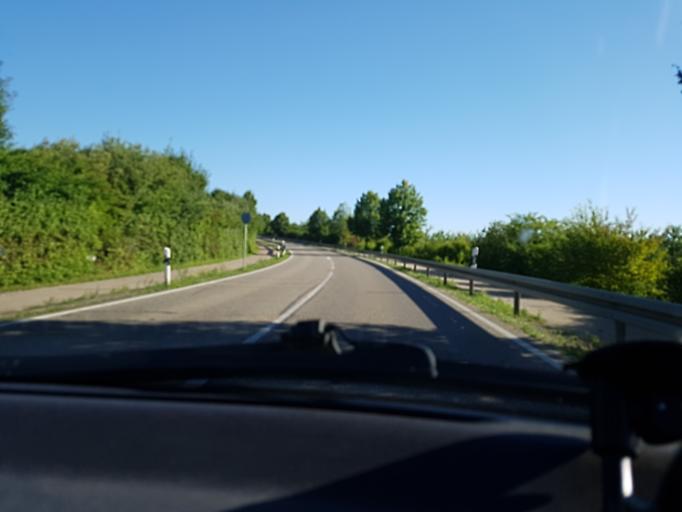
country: DE
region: Baden-Wuerttemberg
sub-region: Freiburg Region
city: Offenburg
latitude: 48.5007
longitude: 7.9624
